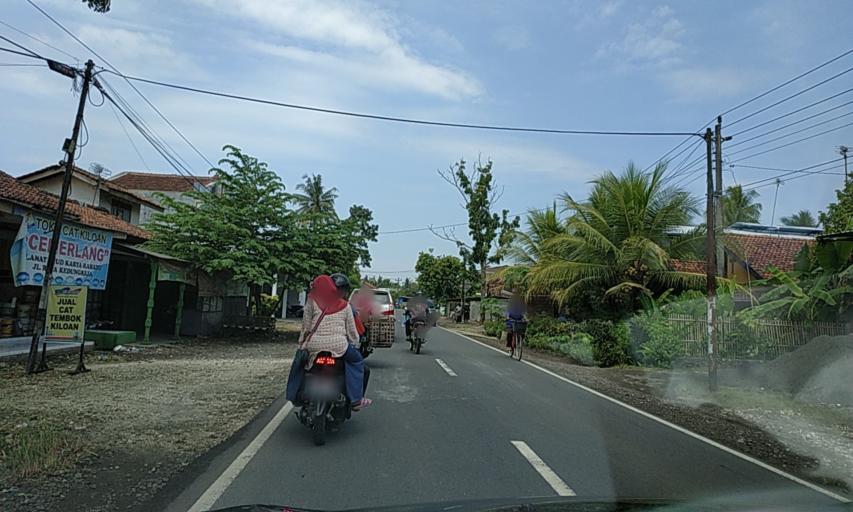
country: ID
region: Central Java
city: Sidareja
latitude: -7.4947
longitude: 108.7898
